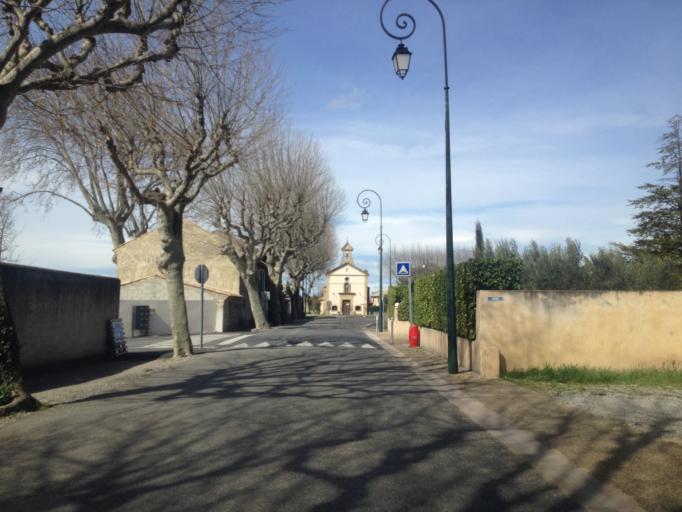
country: FR
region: Provence-Alpes-Cote d'Azur
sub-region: Departement du Vaucluse
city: Camaret-sur-Aigues
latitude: 44.1661
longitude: 4.8715
